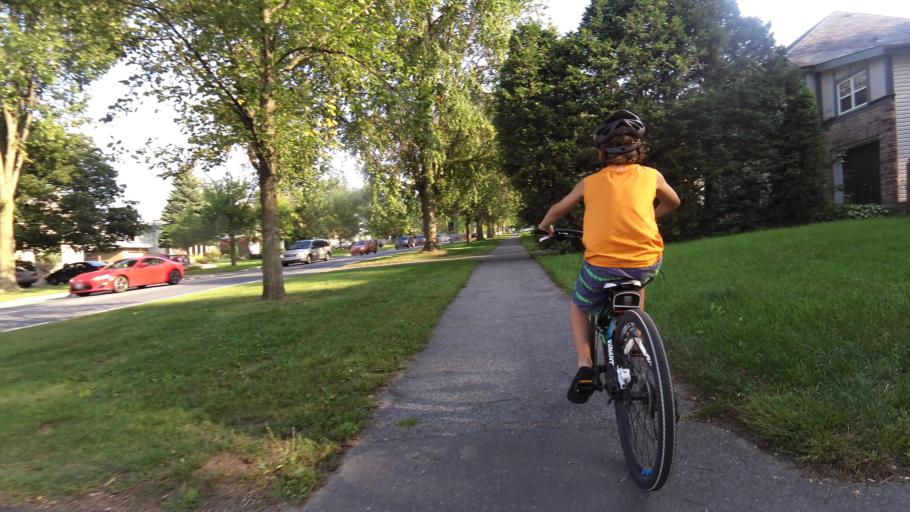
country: CA
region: Ontario
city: Ottawa
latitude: 45.3968
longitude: -75.7420
